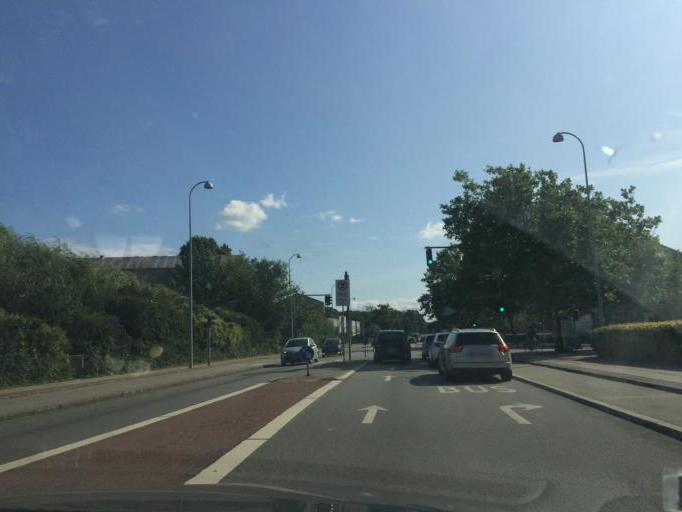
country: DK
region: Capital Region
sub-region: Herlev Kommune
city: Herlev
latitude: 55.7206
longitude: 12.4711
